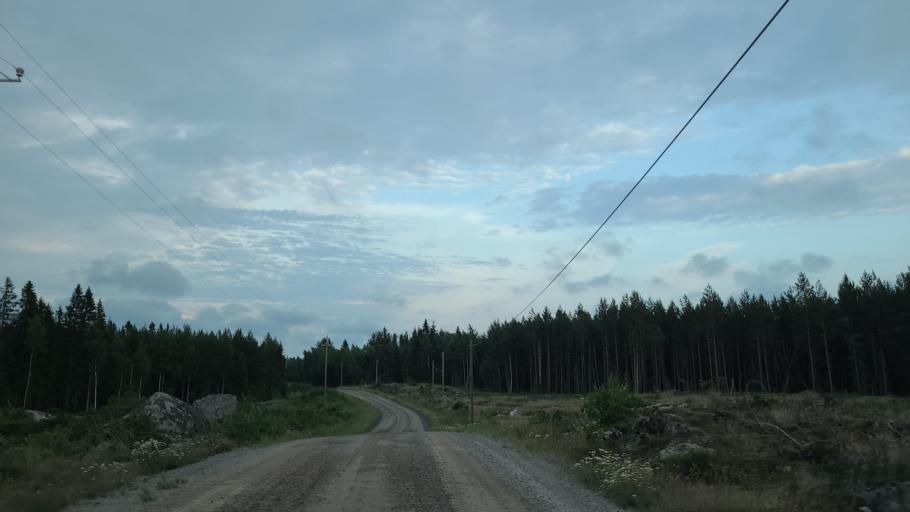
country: FI
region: Ostrobothnia
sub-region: Vaasa
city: Replot
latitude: 63.3174
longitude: 21.1532
